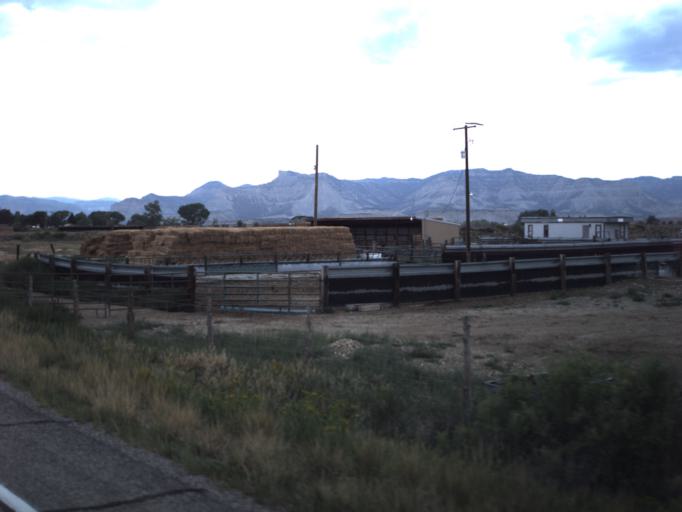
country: US
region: Utah
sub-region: Emery County
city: Huntington
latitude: 39.3449
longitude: -110.9360
